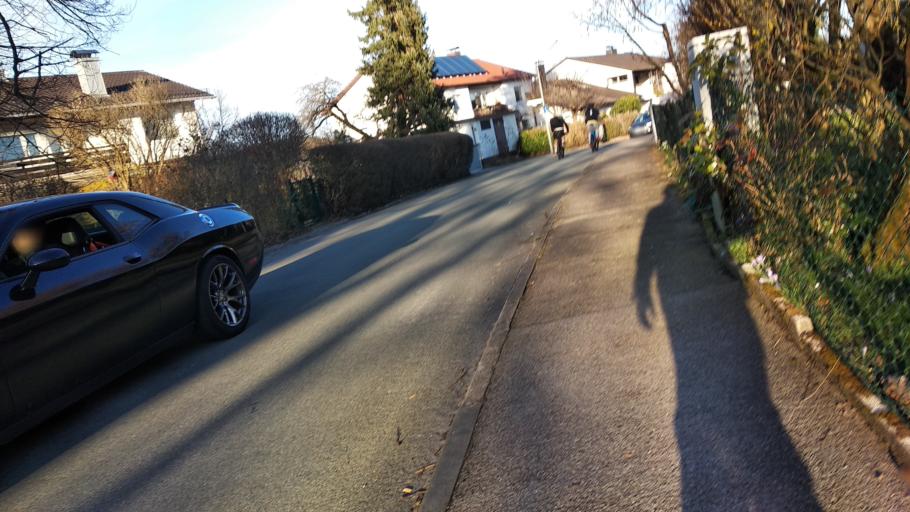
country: DE
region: Bavaria
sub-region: Upper Bavaria
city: Ebersberg
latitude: 48.0807
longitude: 11.9609
